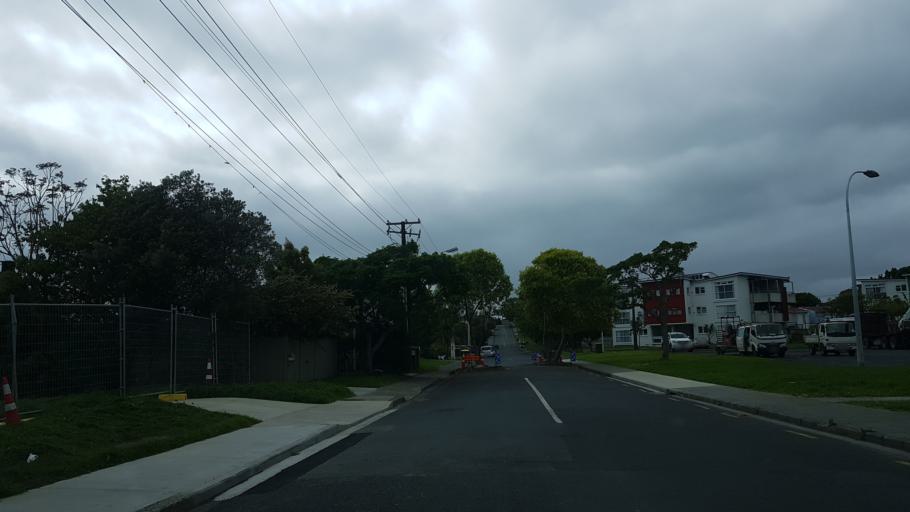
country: NZ
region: Auckland
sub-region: Auckland
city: North Shore
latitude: -36.7963
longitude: 174.7487
